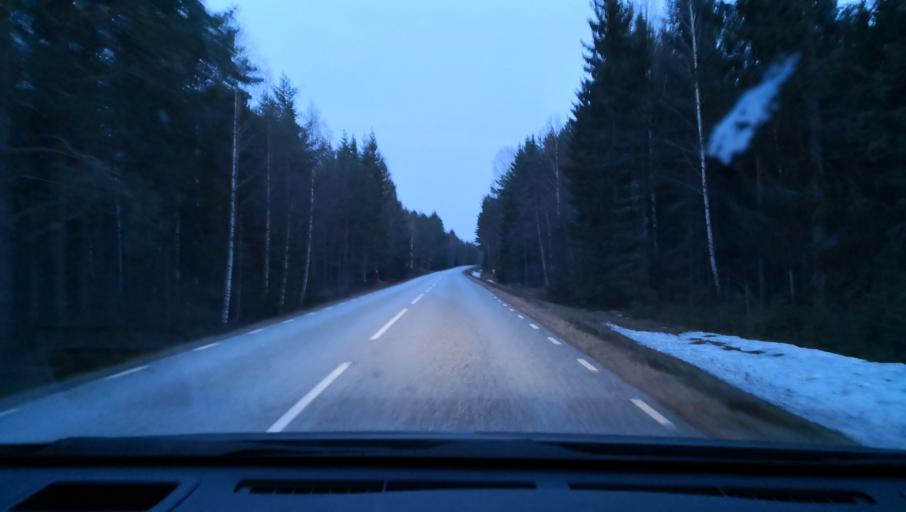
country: SE
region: OErebro
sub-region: Lindesbergs Kommun
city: Frovi
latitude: 59.5959
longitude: 15.3814
